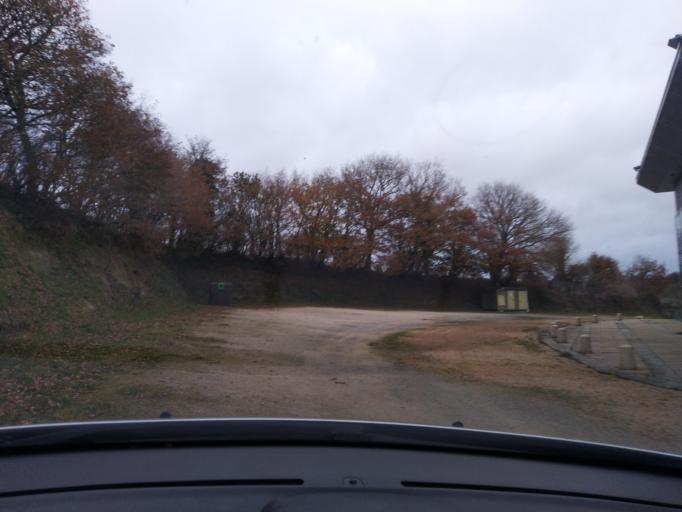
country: FR
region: Brittany
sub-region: Departement du Finistere
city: Guerlesquin
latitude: 48.5090
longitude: -3.5857
